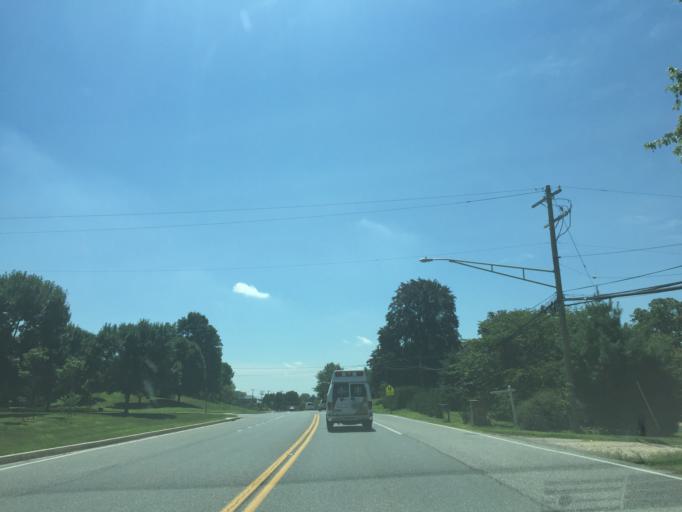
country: US
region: Maryland
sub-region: Harford County
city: Bel Air North
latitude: 39.5815
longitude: -76.3873
